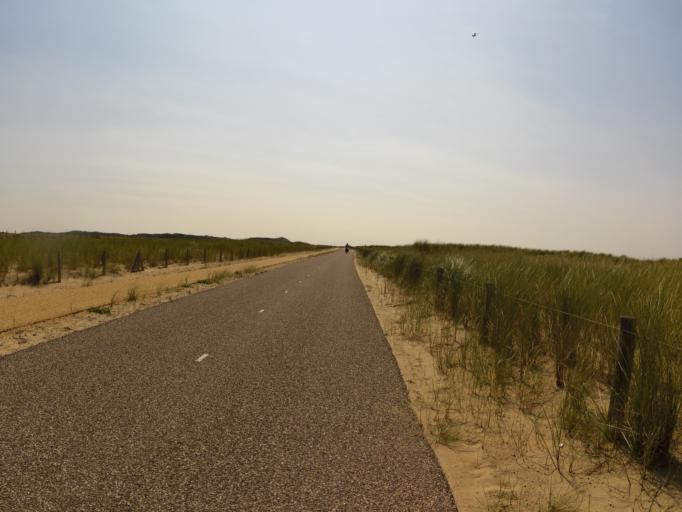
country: NL
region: North Holland
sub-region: Gemeente Bergen
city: Egmond aan Zee
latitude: 52.7362
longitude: 4.6424
